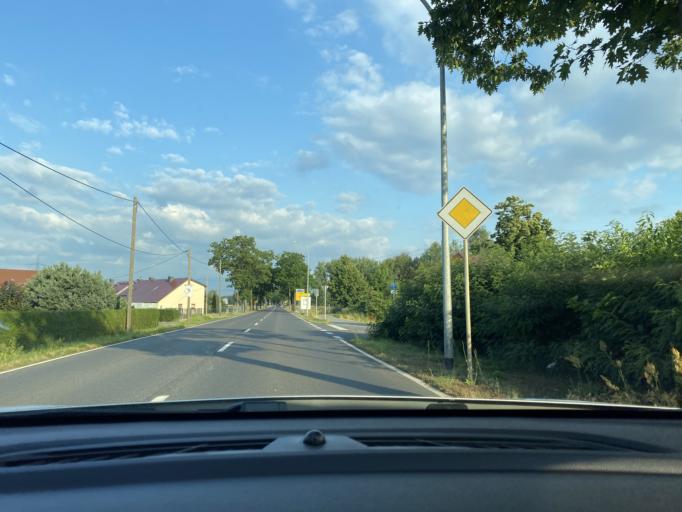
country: DE
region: Saxony
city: Konigswartha
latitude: 51.3493
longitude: 14.3278
